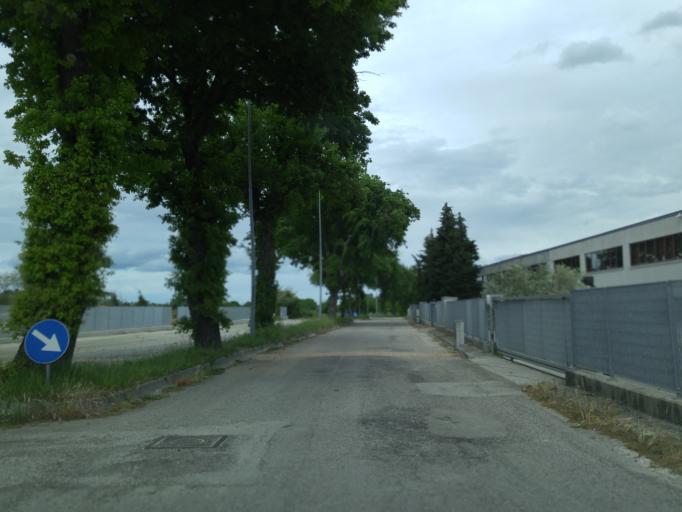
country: IT
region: The Marches
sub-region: Provincia di Pesaro e Urbino
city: Fossombrone
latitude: 43.7015
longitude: 12.8389
